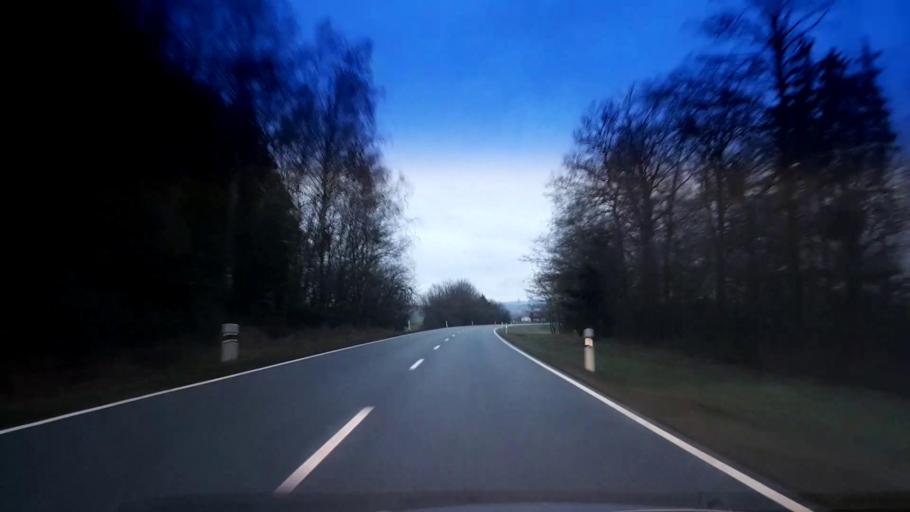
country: DE
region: Bavaria
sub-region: Upper Palatinate
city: Berg
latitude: 49.8438
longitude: 12.1491
